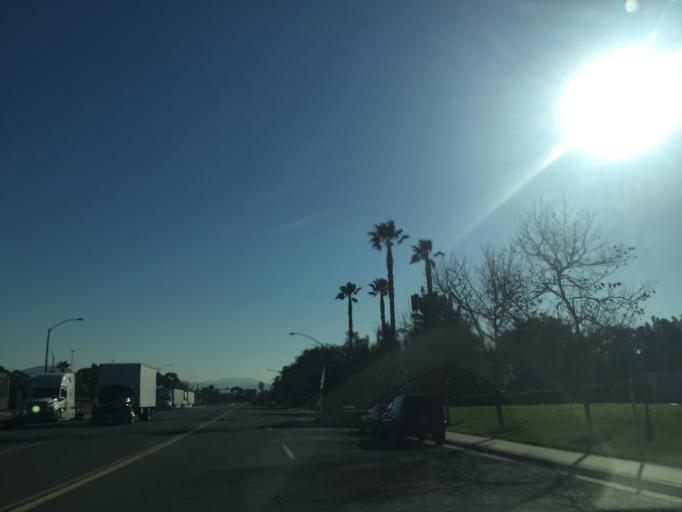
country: MX
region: Baja California
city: Tijuana
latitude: 32.5593
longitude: -116.9279
